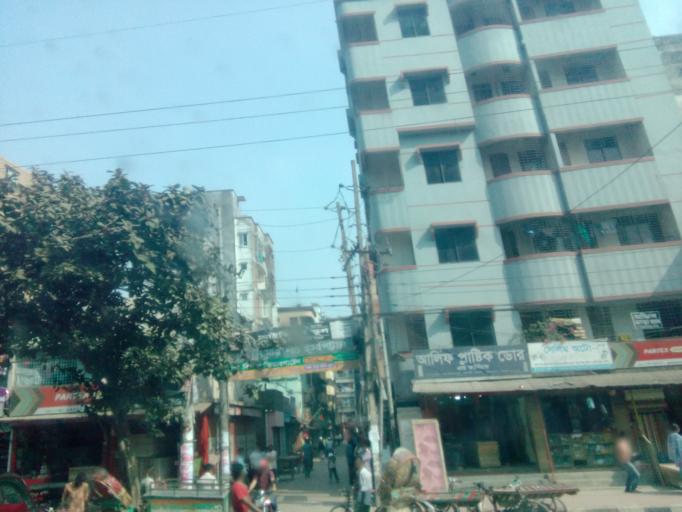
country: BD
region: Dhaka
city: Paltan
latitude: 23.7909
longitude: 90.4250
